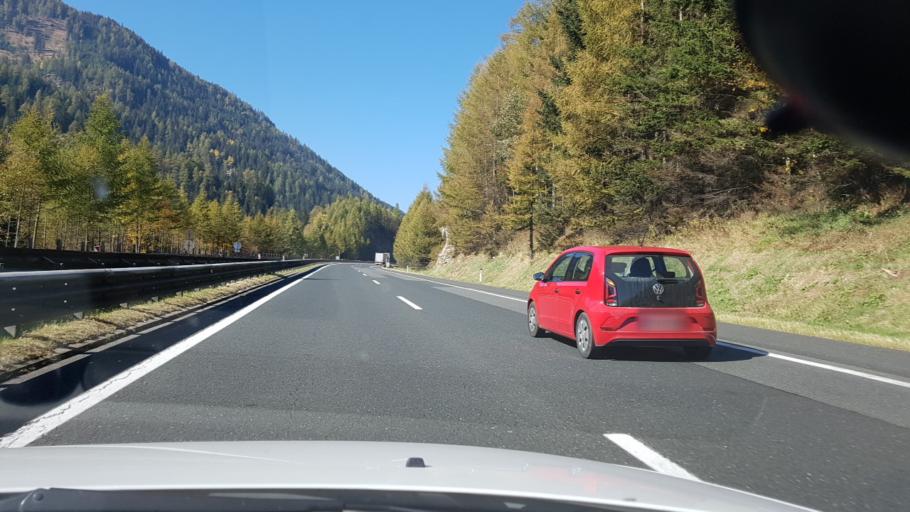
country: AT
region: Salzburg
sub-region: Politischer Bezirk Tamsweg
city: Zederhaus
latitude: 47.1414
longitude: 13.5281
